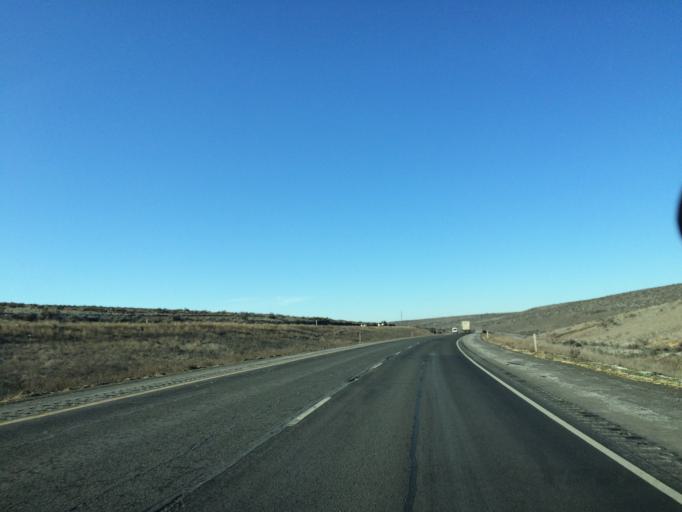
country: US
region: Washington
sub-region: Kittitas County
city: Kittitas
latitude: 46.9479
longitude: -120.2500
